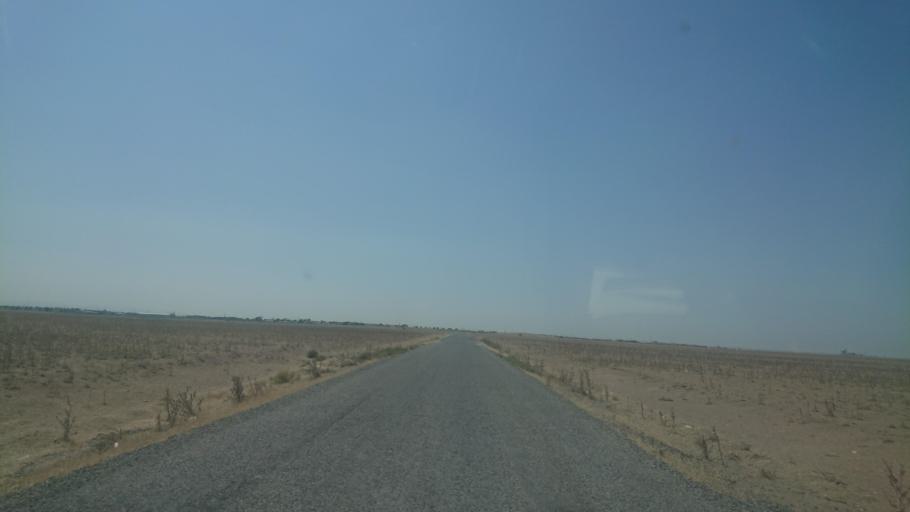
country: TR
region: Aksaray
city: Yesilova
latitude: 38.3058
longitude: 33.7342
